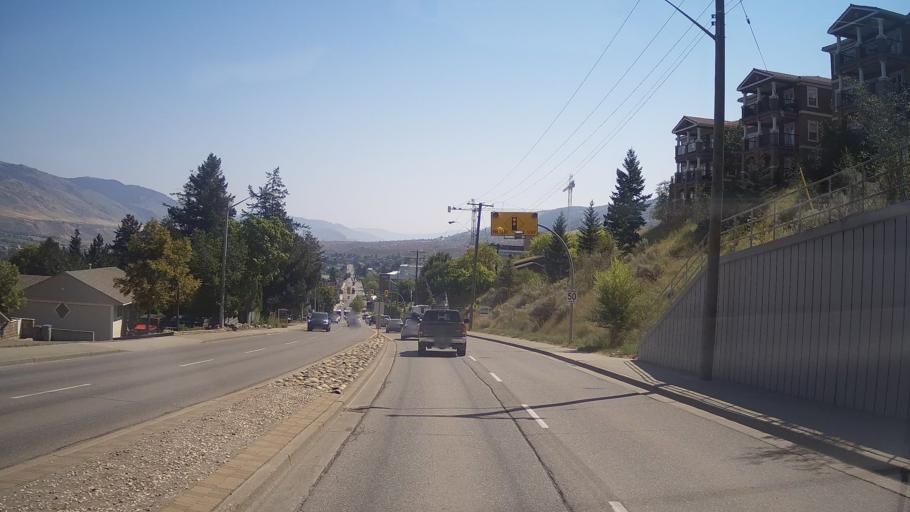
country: CA
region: British Columbia
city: Kamloops
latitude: 50.6715
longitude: -120.3415
